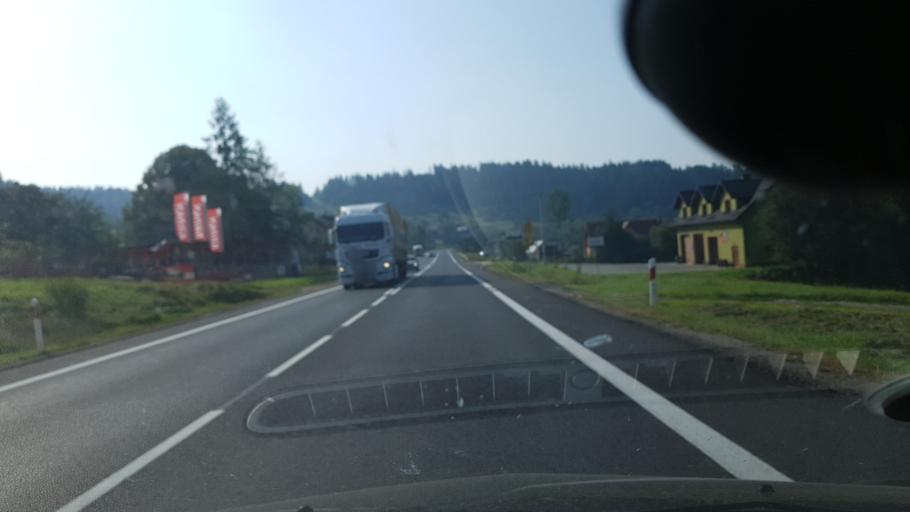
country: PL
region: Lesser Poland Voivodeship
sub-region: Powiat nowotarski
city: Podwilk
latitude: 49.5198
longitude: 19.7197
